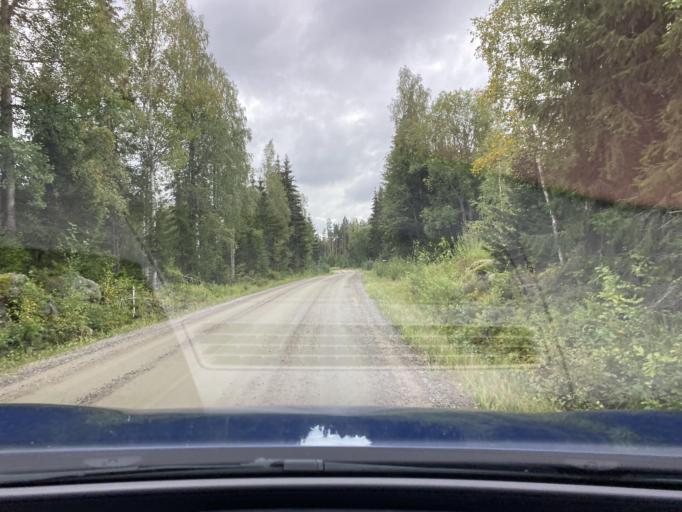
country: FI
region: Pirkanmaa
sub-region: Lounais-Pirkanmaa
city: Punkalaidun
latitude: 61.2006
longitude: 23.1783
